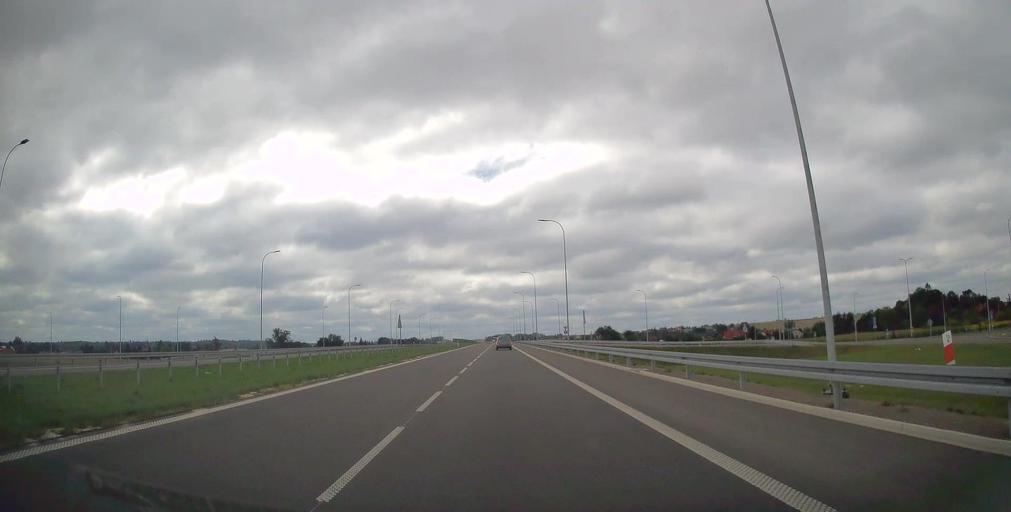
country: PL
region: Lesser Poland Voivodeship
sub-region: Powiat krakowski
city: Slomniki
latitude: 50.2262
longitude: 20.0131
